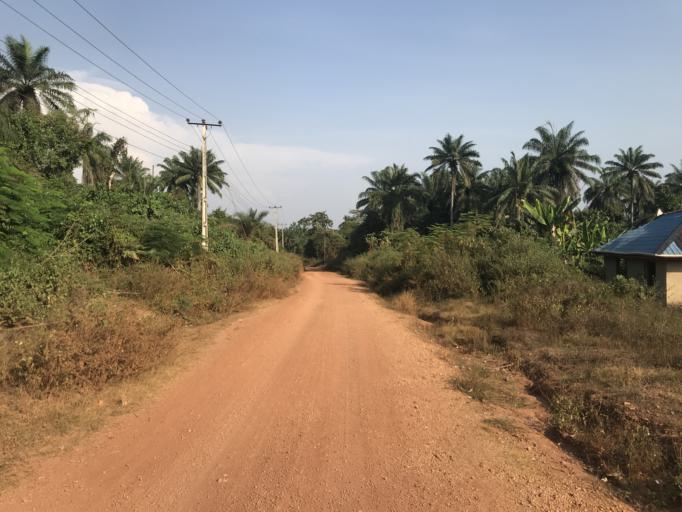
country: NG
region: Osun
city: Bode Osi
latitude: 7.7673
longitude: 4.3077
